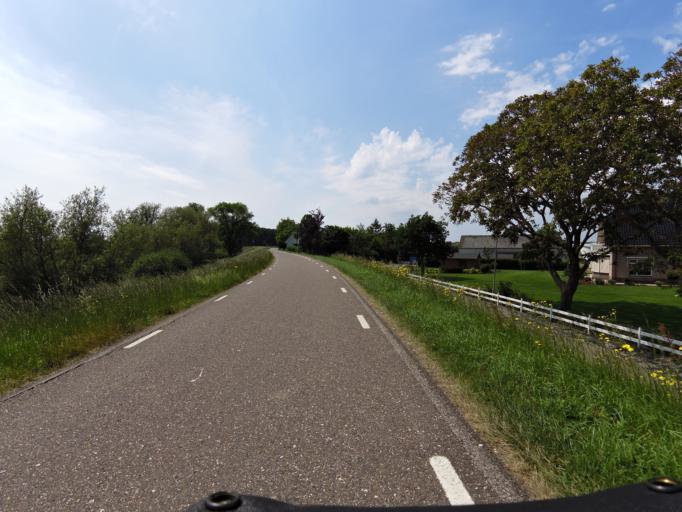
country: NL
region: North Brabant
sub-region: Gemeente Aalburg
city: Aalburg
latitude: 51.7902
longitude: 5.0916
